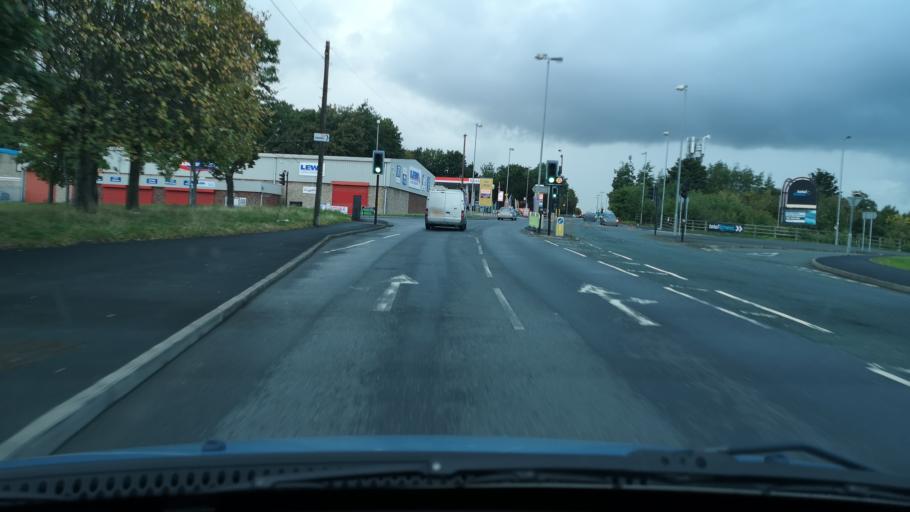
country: GB
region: England
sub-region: City and Borough of Wakefield
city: Horbury
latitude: 53.6806
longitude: -1.5467
